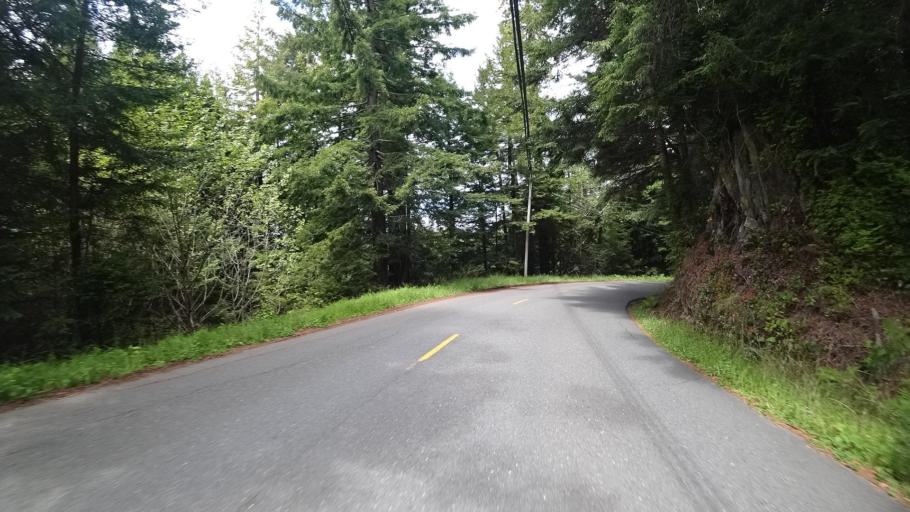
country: US
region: California
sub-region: Humboldt County
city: Bayside
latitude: 40.7852
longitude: -124.0578
